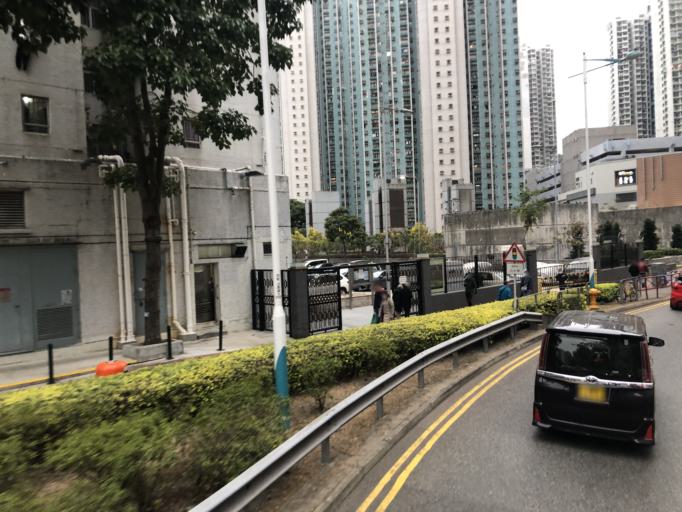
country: HK
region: Sai Kung
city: Sai Kung
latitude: 22.3158
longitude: 114.2637
